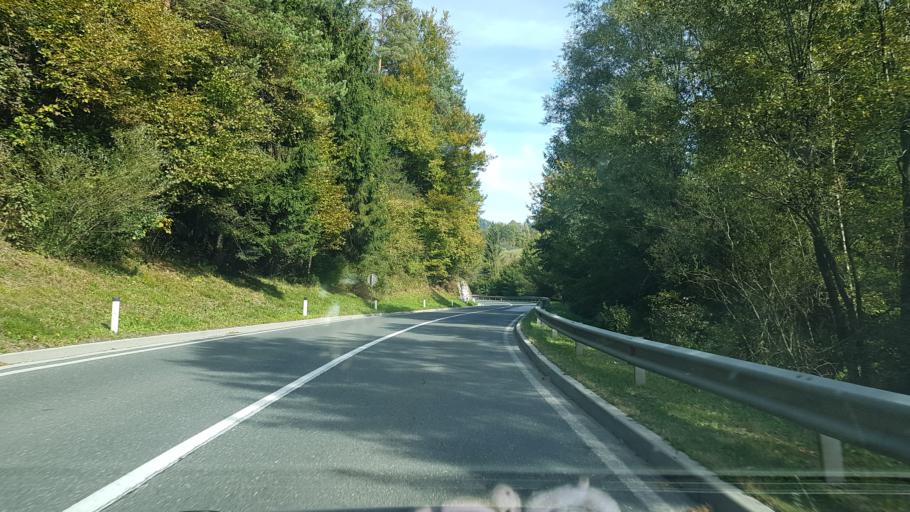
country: SI
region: Mislinja
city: Mislinja
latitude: 46.4382
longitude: 15.1937
